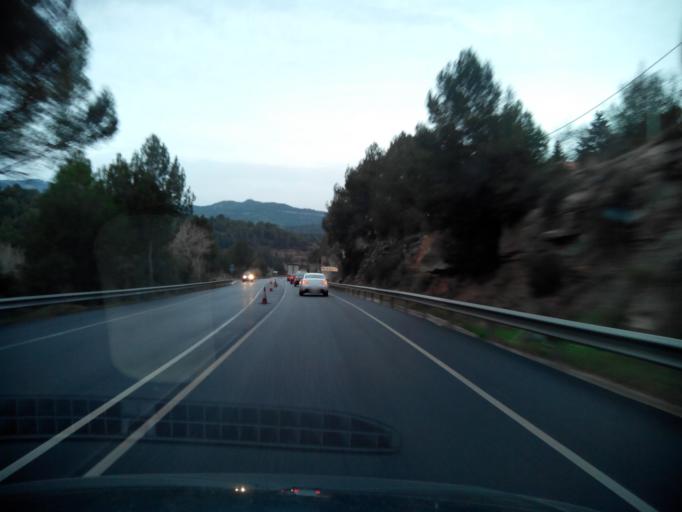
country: ES
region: Catalonia
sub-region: Provincia de Barcelona
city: Monistrol de Montserrat
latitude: 41.6151
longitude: 1.8708
